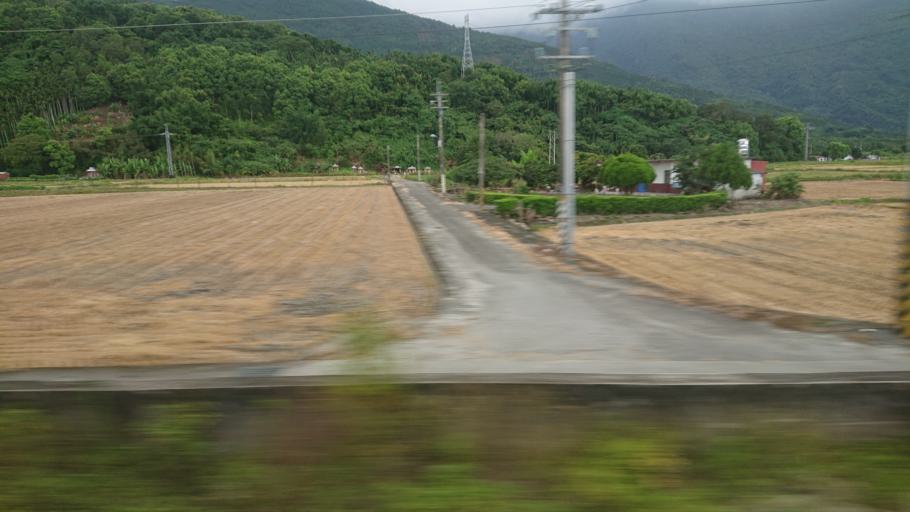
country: TW
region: Taiwan
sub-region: Hualien
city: Hualian
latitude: 23.7334
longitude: 121.4403
